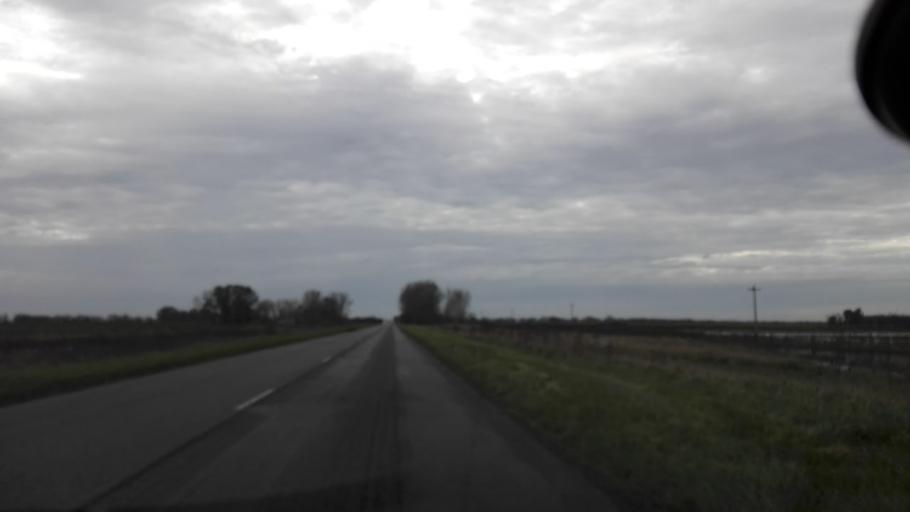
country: AR
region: Buenos Aires
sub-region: Partido de Rauch
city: Rauch
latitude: -36.4841
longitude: -59.0274
